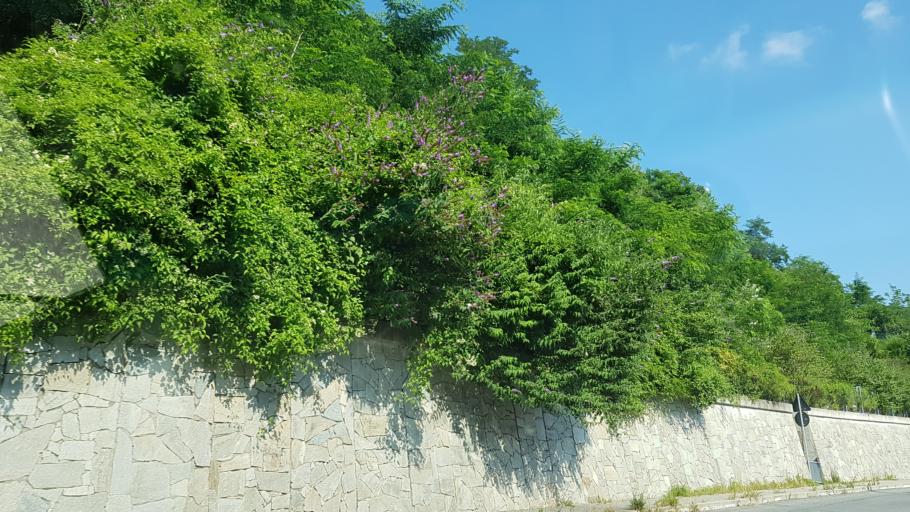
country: IT
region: Liguria
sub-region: Provincia di Genova
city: Pedemonte
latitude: 44.4931
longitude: 8.9206
